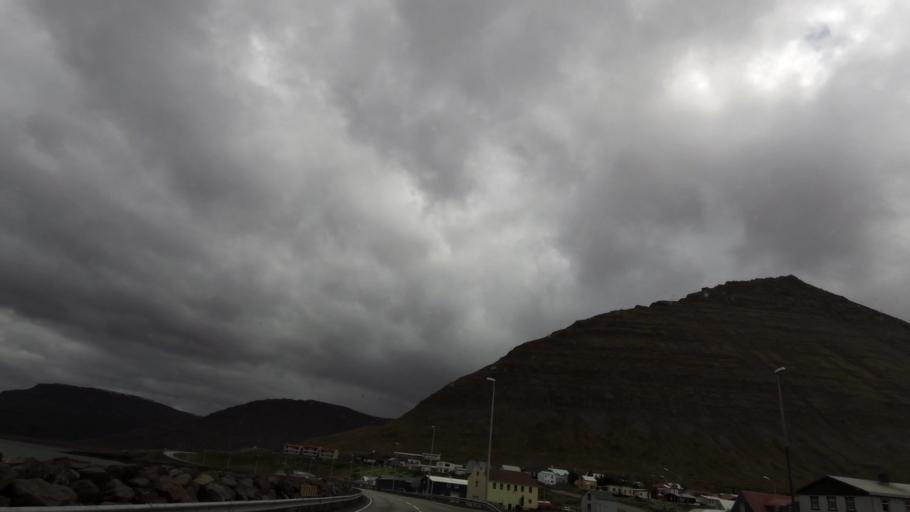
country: IS
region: Westfjords
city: Isafjoerdur
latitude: 66.1121
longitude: -23.1211
